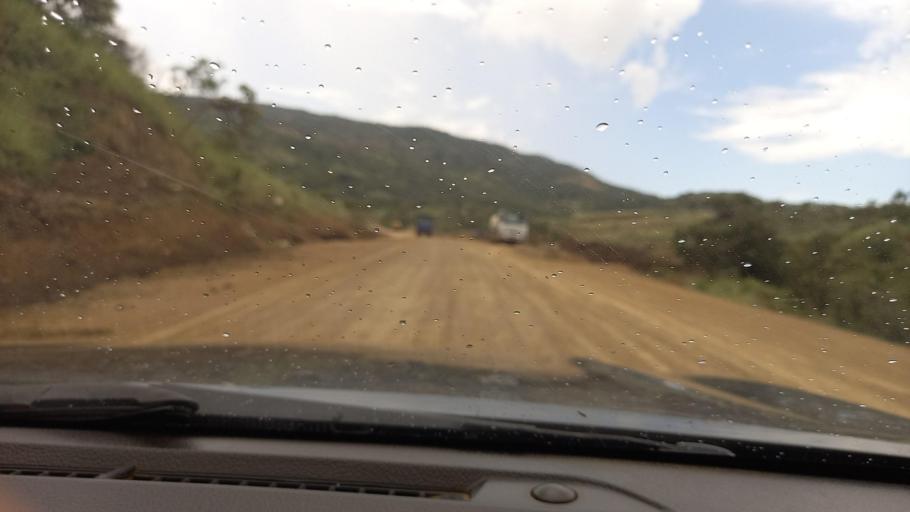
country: ET
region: Southern Nations, Nationalities, and People's Region
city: Mizan Teferi
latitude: 6.1922
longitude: 35.6743
